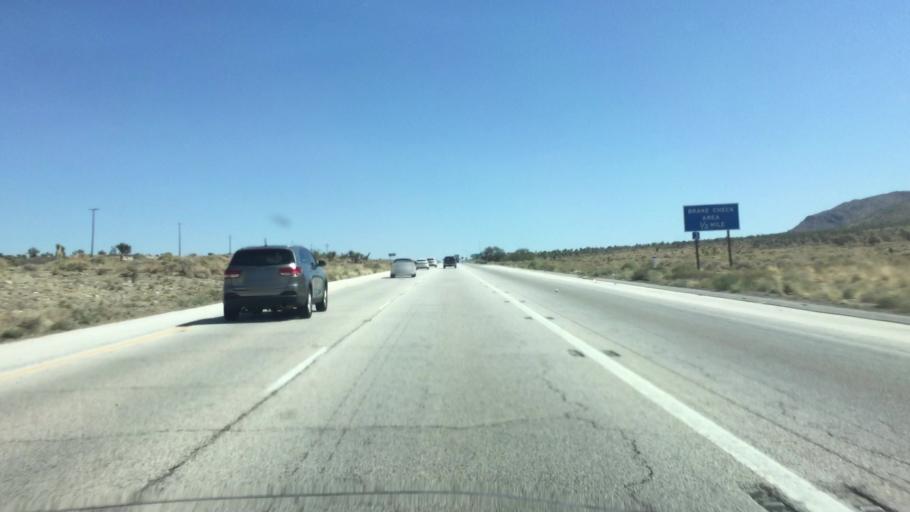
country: US
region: Nevada
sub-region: Clark County
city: Sandy Valley
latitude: 35.4715
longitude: -115.5584
